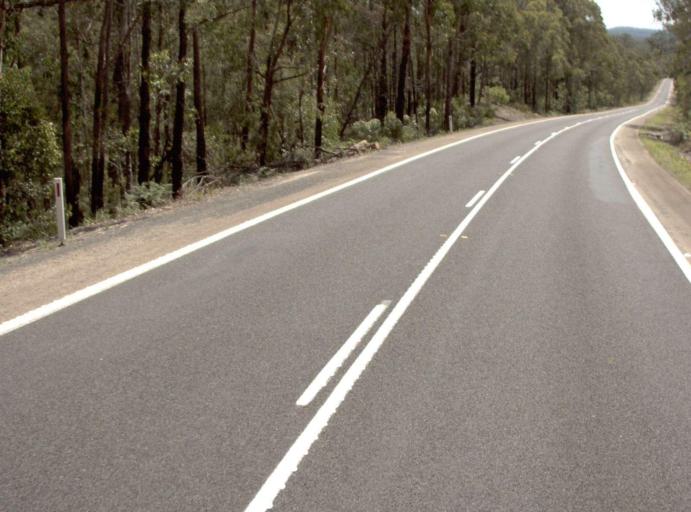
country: AU
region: New South Wales
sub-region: Bombala
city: Bombala
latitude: -37.5667
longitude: 149.0970
